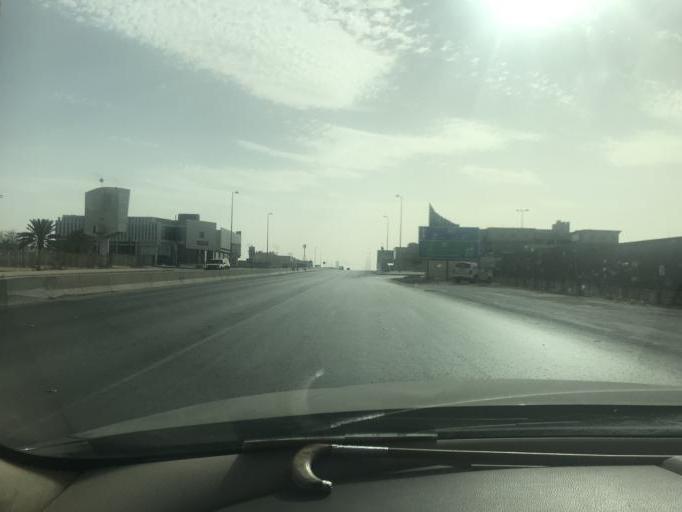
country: SA
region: Ar Riyad
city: Riyadh
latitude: 24.8185
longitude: 46.6891
